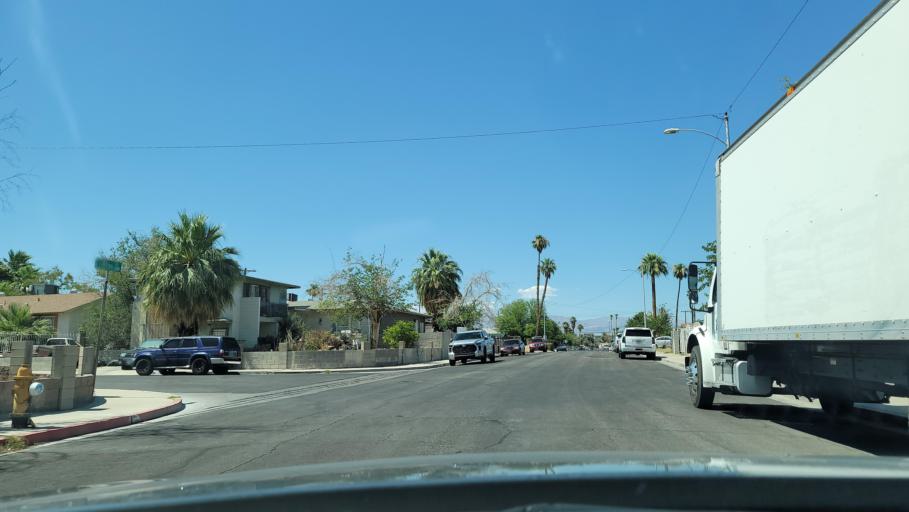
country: US
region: Nevada
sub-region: Clark County
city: Las Vegas
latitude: 36.1795
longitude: -115.1237
